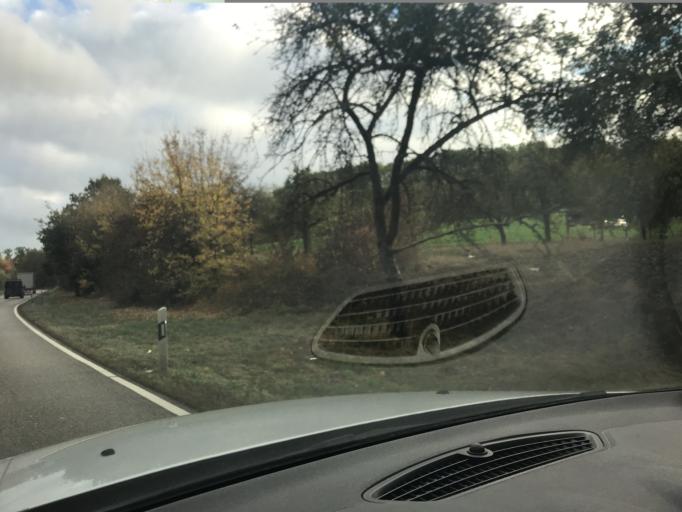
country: DE
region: Baden-Wuerttemberg
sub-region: Regierungsbezirk Stuttgart
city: Grossbottwar
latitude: 48.9913
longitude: 9.3047
